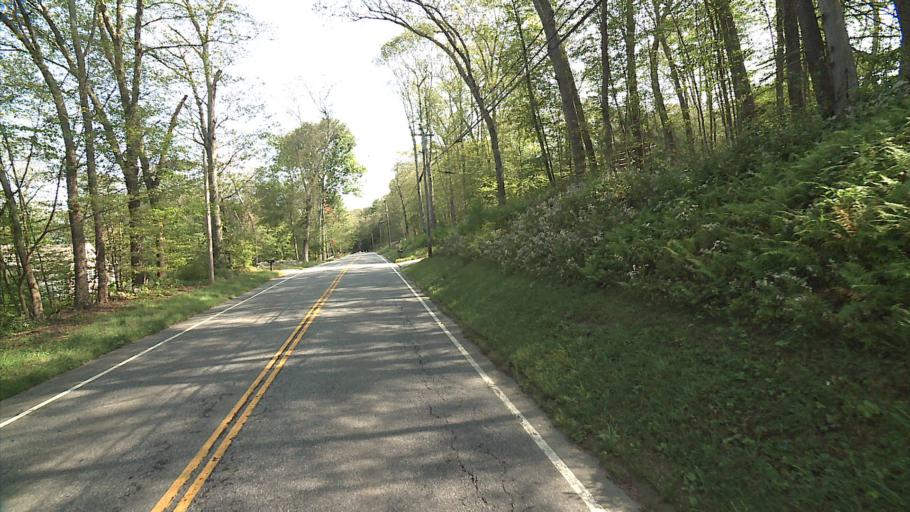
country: US
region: Connecticut
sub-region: New London County
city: Jewett City
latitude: 41.6345
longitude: -71.9972
